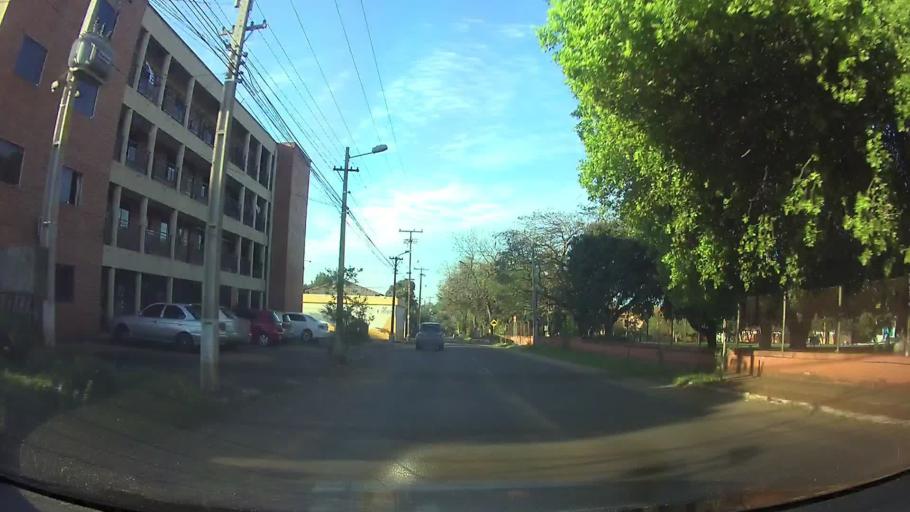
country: PY
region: Central
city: Fernando de la Mora
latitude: -25.3406
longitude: -57.5312
